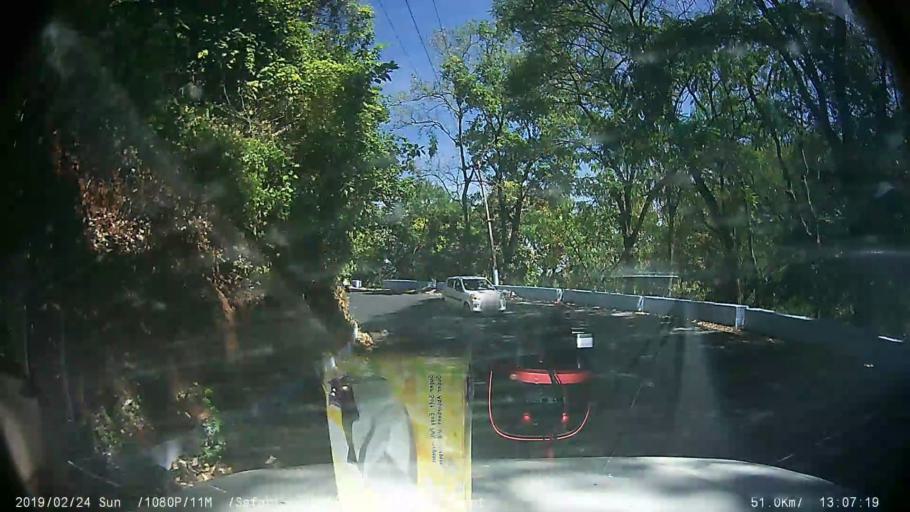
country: IN
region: Tamil Nadu
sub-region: Nilgiri
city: Wellington
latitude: 11.3375
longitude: 76.8337
